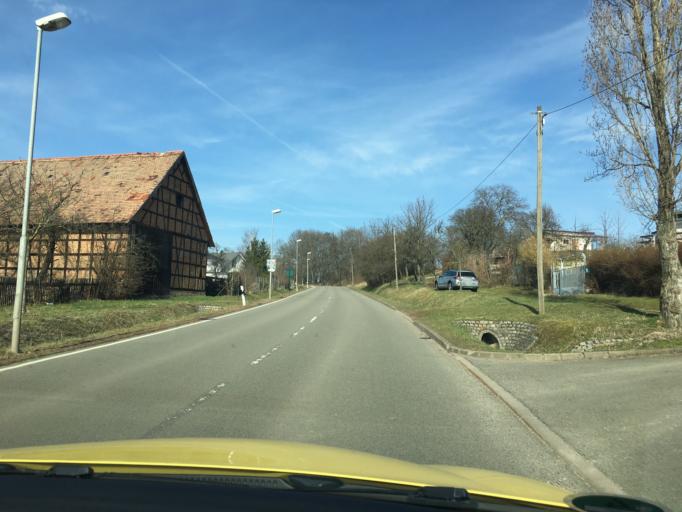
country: DE
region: Thuringia
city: Ollendorf
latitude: 51.0365
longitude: 11.1908
